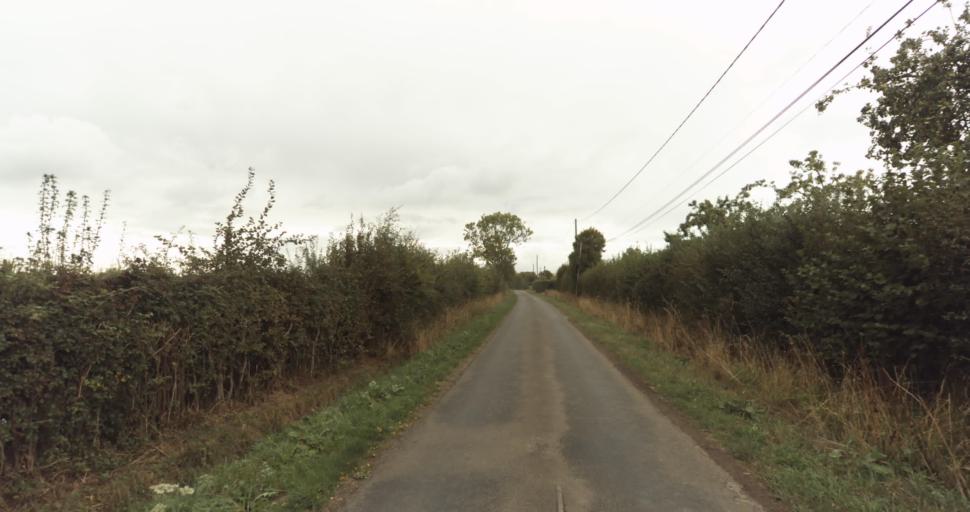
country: FR
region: Lower Normandy
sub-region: Departement de l'Orne
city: Gace
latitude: 48.8495
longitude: 0.3215
